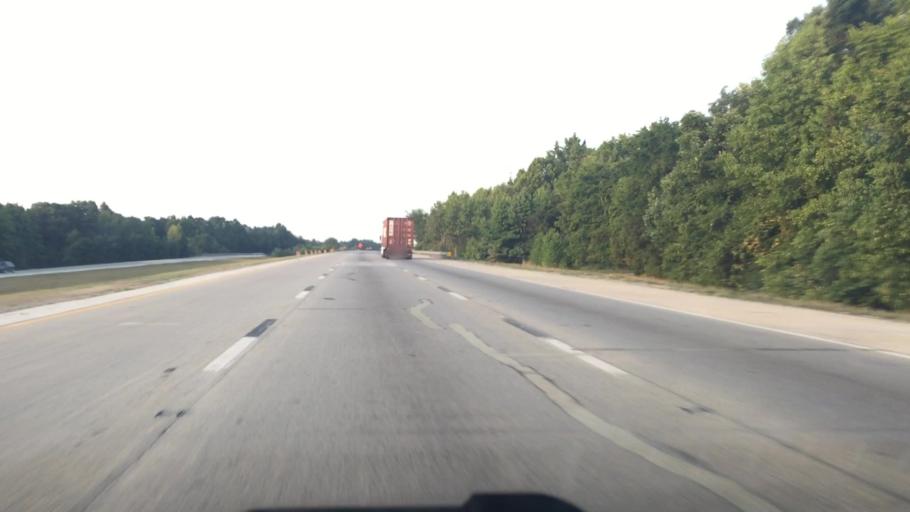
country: US
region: North Carolina
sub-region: Guilford County
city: Jamestown
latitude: 35.9656
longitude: -79.8935
